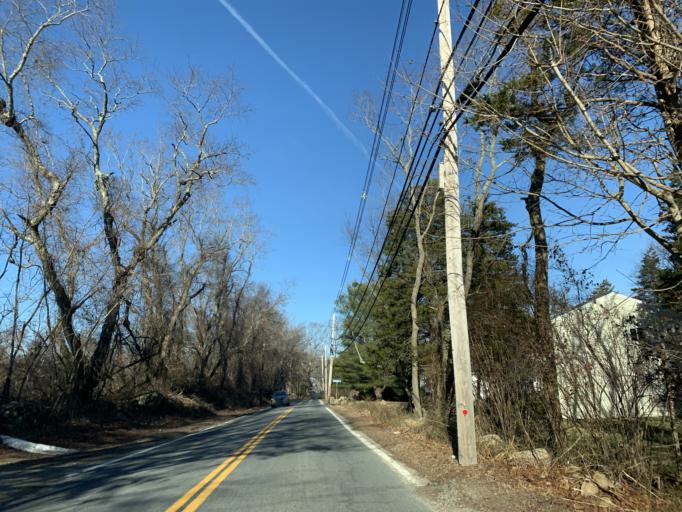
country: US
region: Rhode Island
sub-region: Washington County
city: Exeter
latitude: 41.5753
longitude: -71.5341
